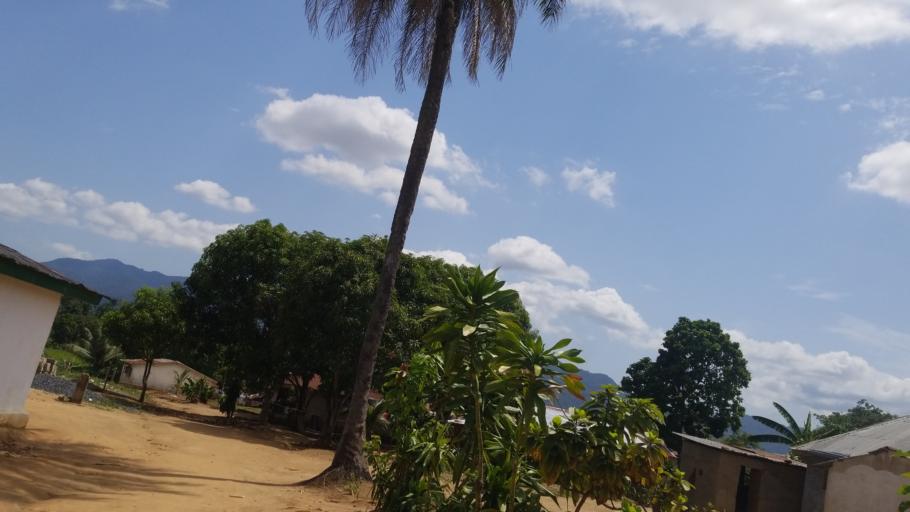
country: SL
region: Western Area
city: Waterloo
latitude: 8.3107
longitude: -13.0576
